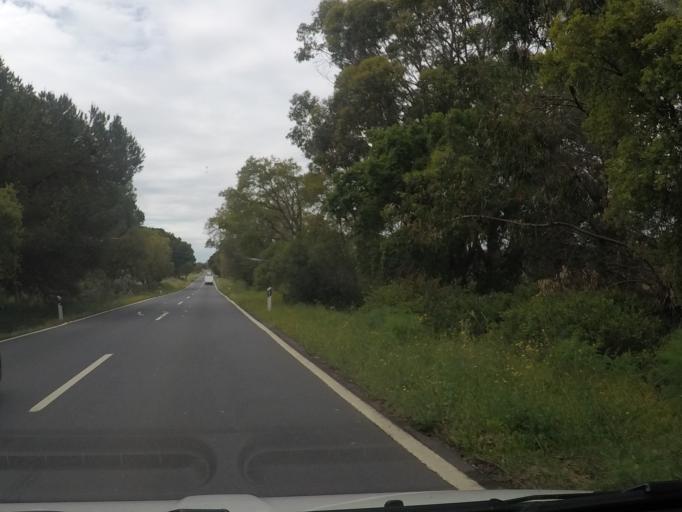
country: PT
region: Setubal
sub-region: Sines
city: Porto Covo
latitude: 37.8826
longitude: -8.7489
